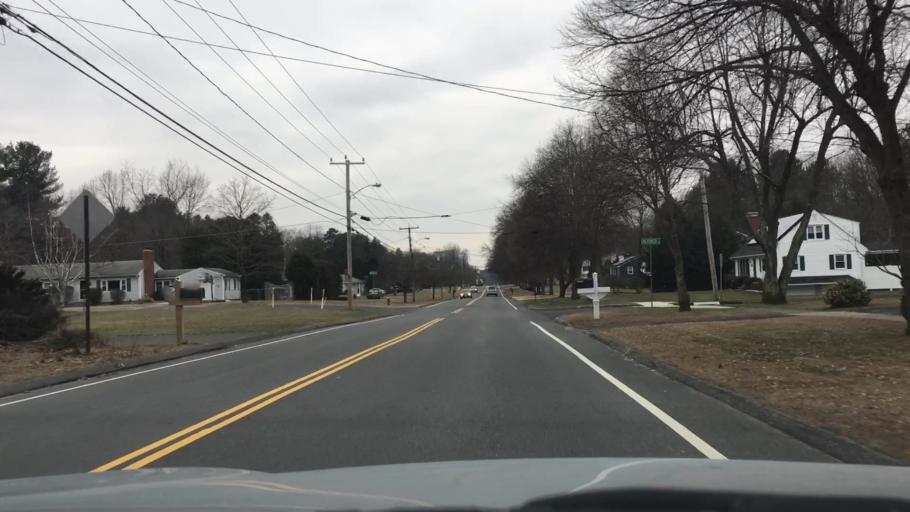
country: US
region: Connecticut
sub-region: Hartford County
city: Sherwood Manor
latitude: 42.0387
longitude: -72.5472
